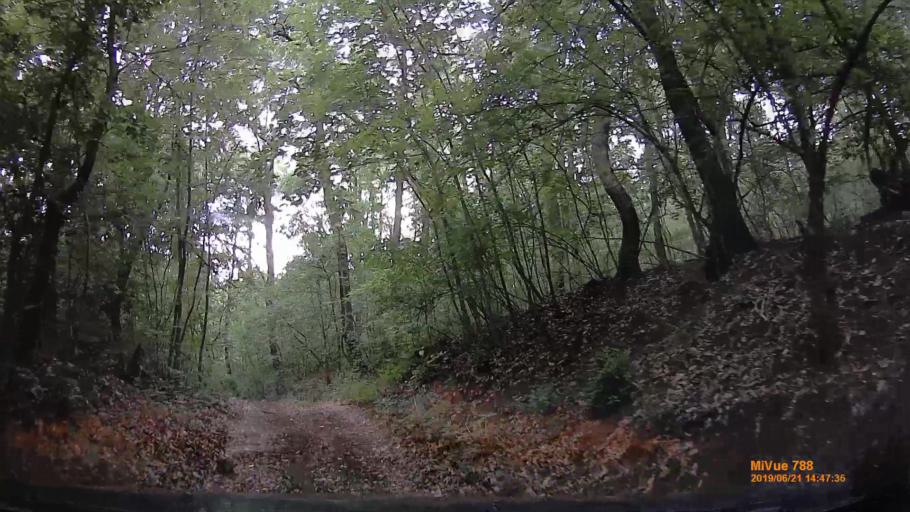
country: HU
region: Baranya
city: Hosszuheteny
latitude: 46.1313
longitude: 18.3082
